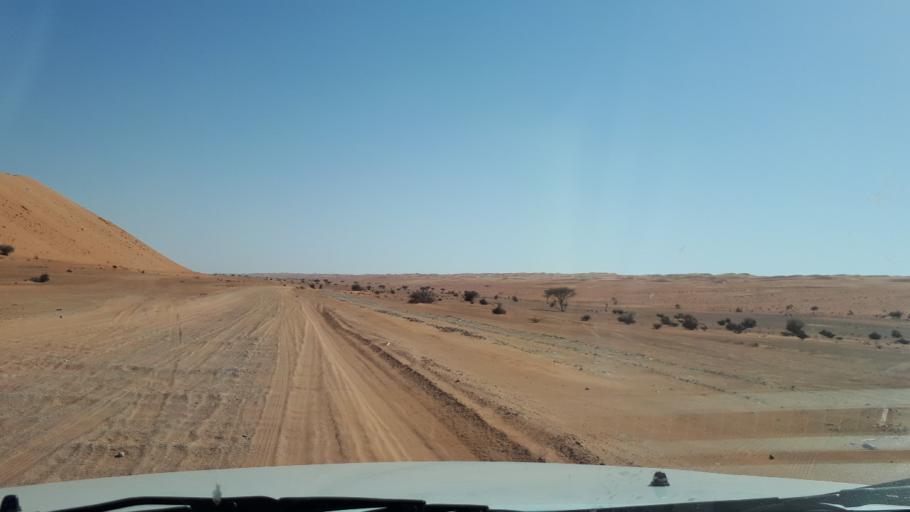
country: OM
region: Ash Sharqiyah
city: Badiyah
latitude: 22.4573
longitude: 58.7401
